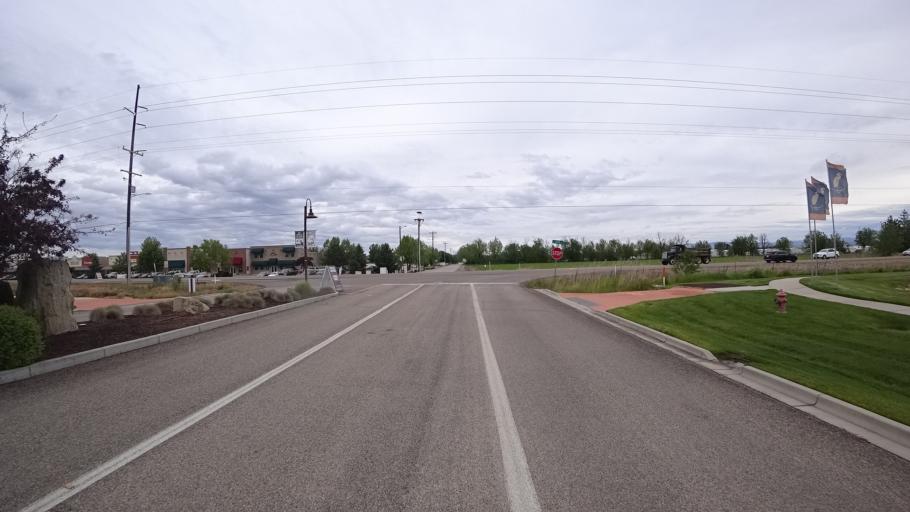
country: US
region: Idaho
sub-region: Ada County
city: Star
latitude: 43.6915
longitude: -116.4732
